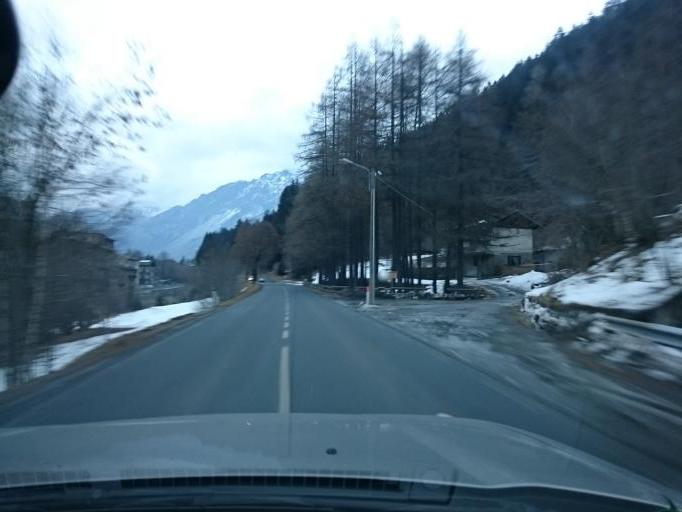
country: IT
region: Lombardy
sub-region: Provincia di Sondrio
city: Valdisotto
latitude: 46.4257
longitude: 10.3563
